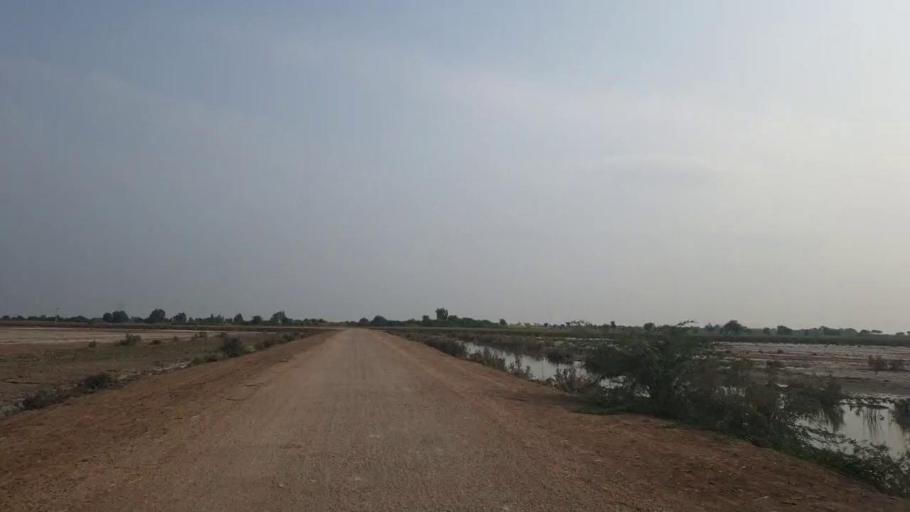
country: PK
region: Sindh
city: Badin
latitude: 24.6016
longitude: 68.6968
